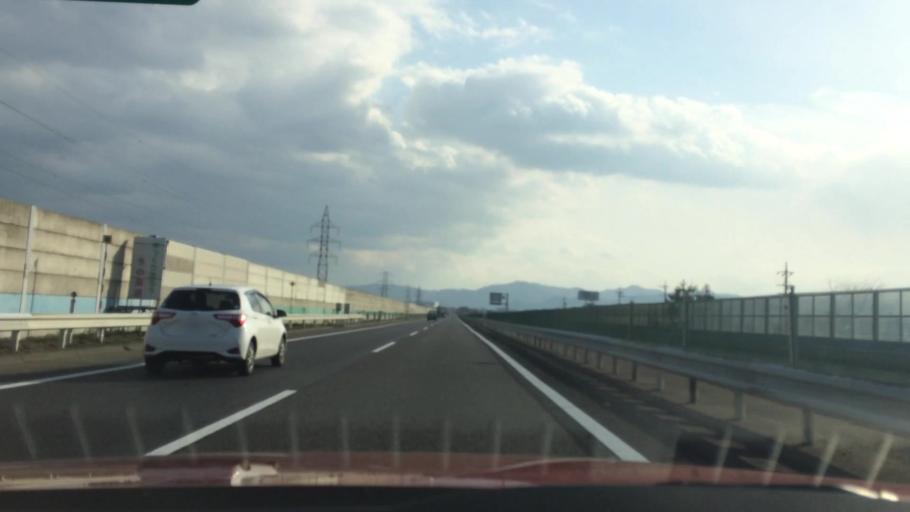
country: JP
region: Nagano
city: Matsumoto
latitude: 36.1850
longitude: 137.9386
